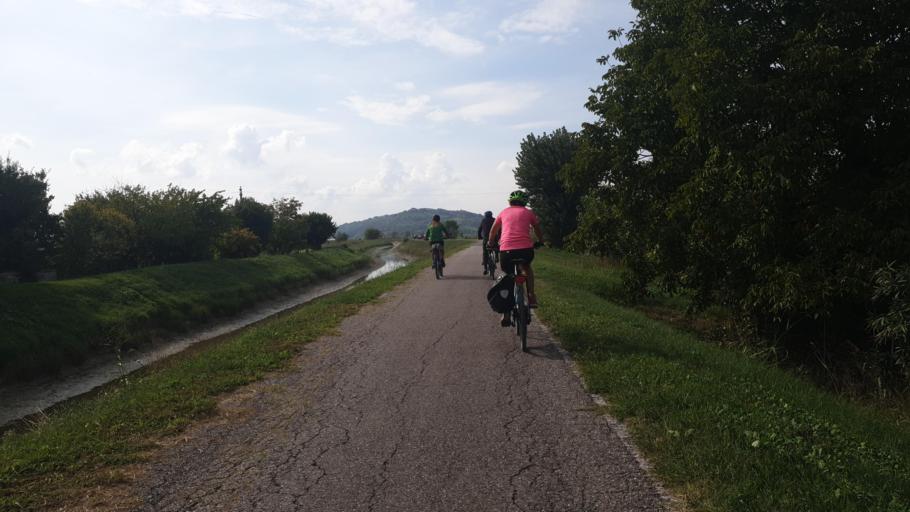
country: IT
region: Veneto
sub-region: Provincia di Padova
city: Bastia
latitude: 45.3716
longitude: 11.6342
